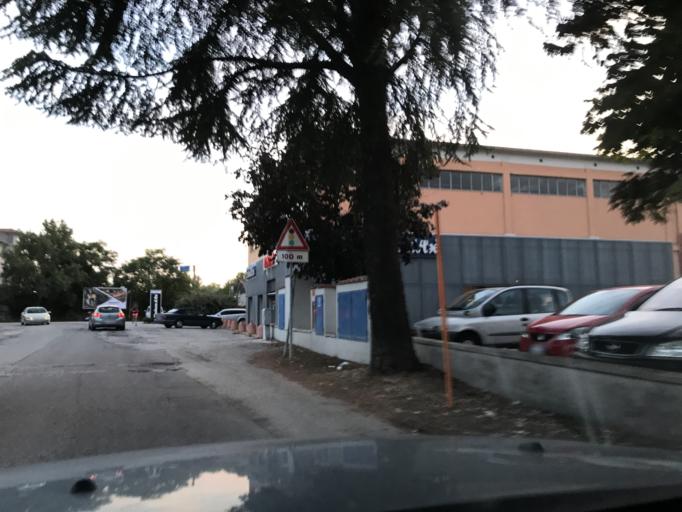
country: IT
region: Umbria
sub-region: Provincia di Perugia
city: Via Lippia
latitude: 43.0898
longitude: 12.4504
